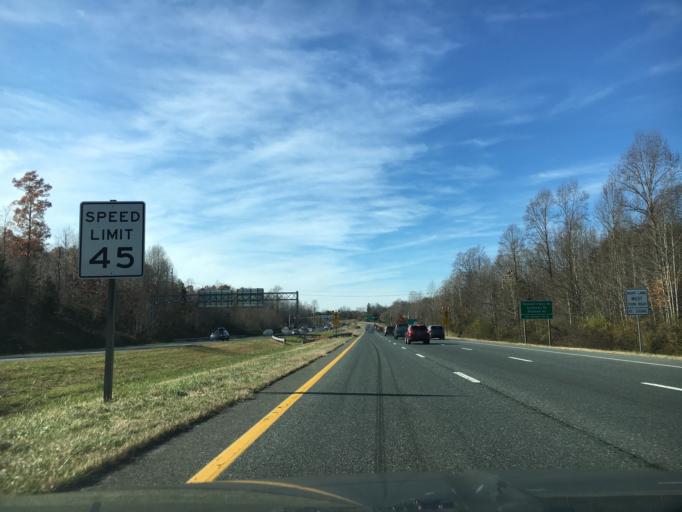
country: US
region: Virginia
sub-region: Amherst County
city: Madison Heights
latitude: 37.3860
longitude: -79.0971
